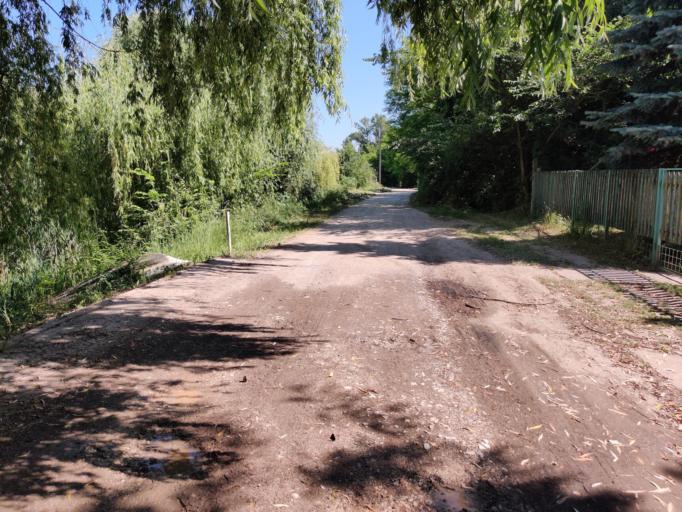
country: HU
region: Hajdu-Bihar
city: Balmazujvaros
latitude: 47.6022
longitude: 21.3784
